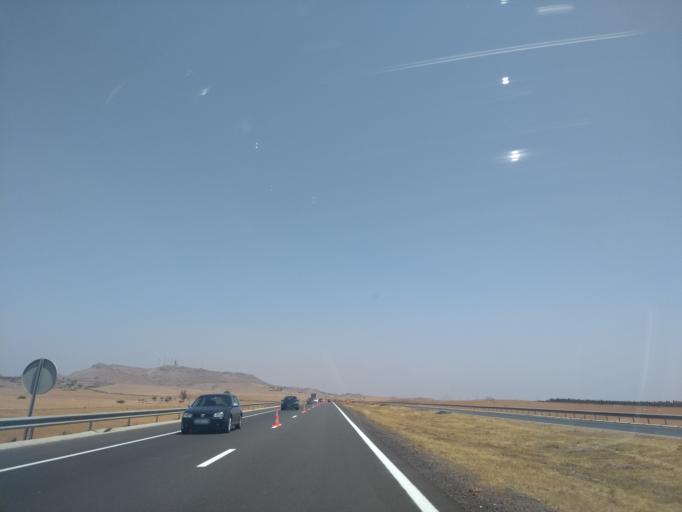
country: MA
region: Marrakech-Tensift-Al Haouz
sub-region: Kelaa-Des-Sraghna
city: Sidi Abdallah
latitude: 32.4467
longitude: -7.9316
